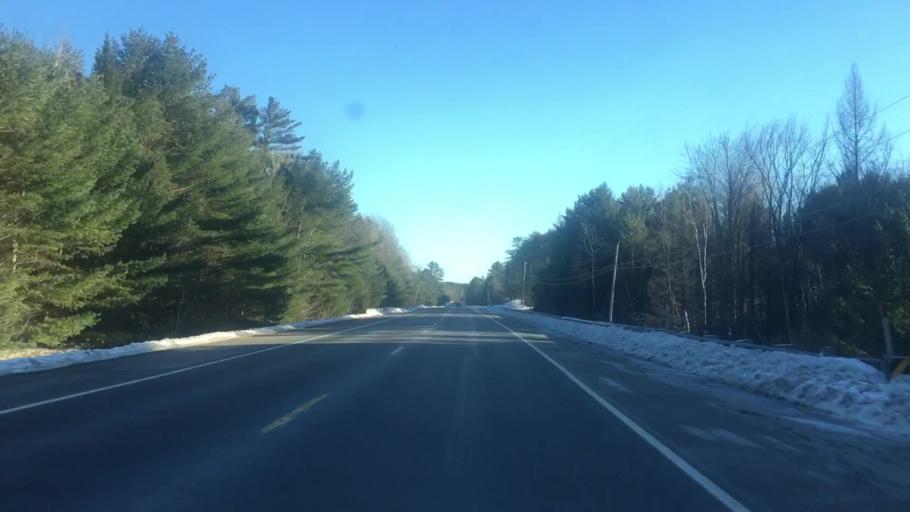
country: US
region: Maine
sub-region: Somerset County
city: Norridgewock
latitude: 44.6916
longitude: -69.7434
